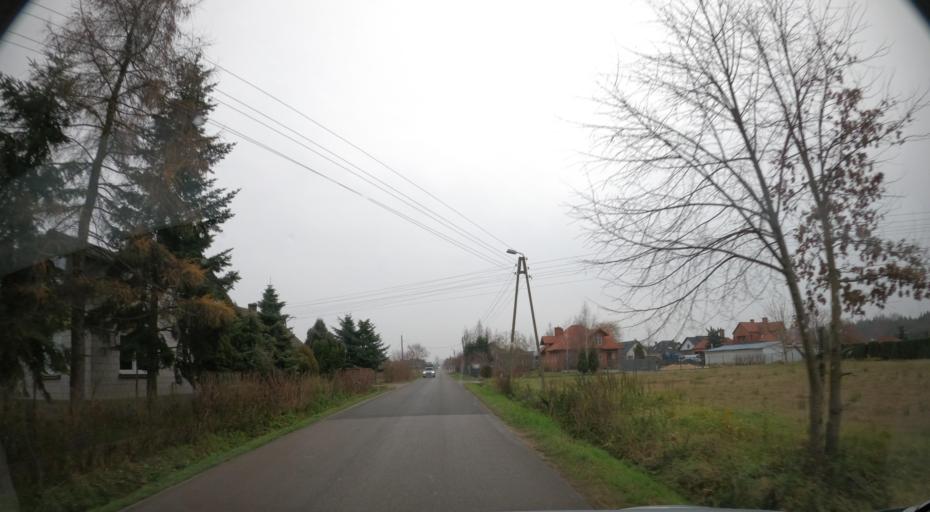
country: PL
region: Masovian Voivodeship
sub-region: Powiat radomski
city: Jastrzebia
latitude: 51.4236
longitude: 21.2389
